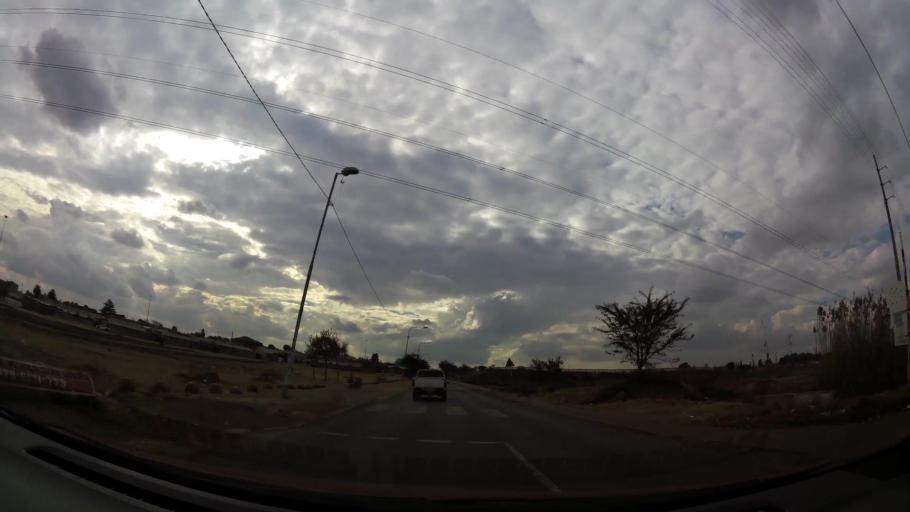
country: ZA
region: Gauteng
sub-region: City of Johannesburg Metropolitan Municipality
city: Soweto
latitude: -26.2460
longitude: 27.8407
